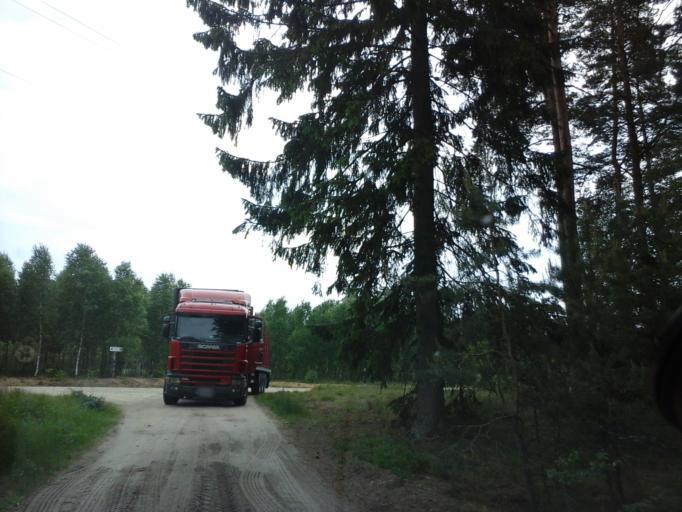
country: PL
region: West Pomeranian Voivodeship
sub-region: Powiat choszczenski
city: Drawno
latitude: 53.1390
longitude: 15.7330
